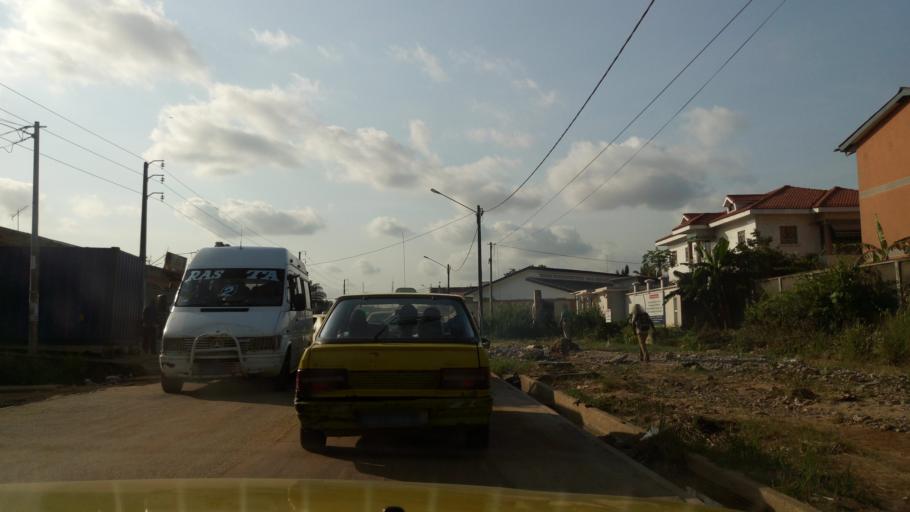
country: CI
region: Lagunes
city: Abidjan
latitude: 5.3623
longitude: -3.9624
